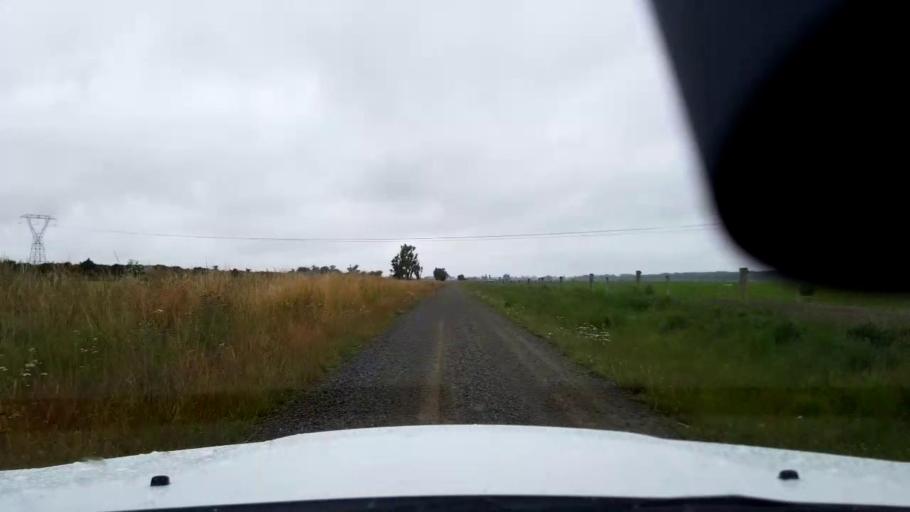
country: NZ
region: Canterbury
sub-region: Timaru District
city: Pleasant Point
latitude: -44.2543
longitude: 171.1835
